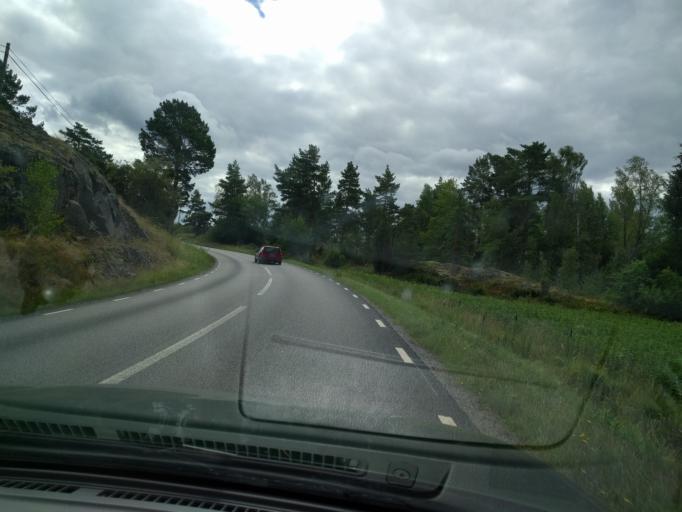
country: SE
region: Soedermanland
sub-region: Nykopings Kommun
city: Svalsta
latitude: 58.5178
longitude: 16.8460
